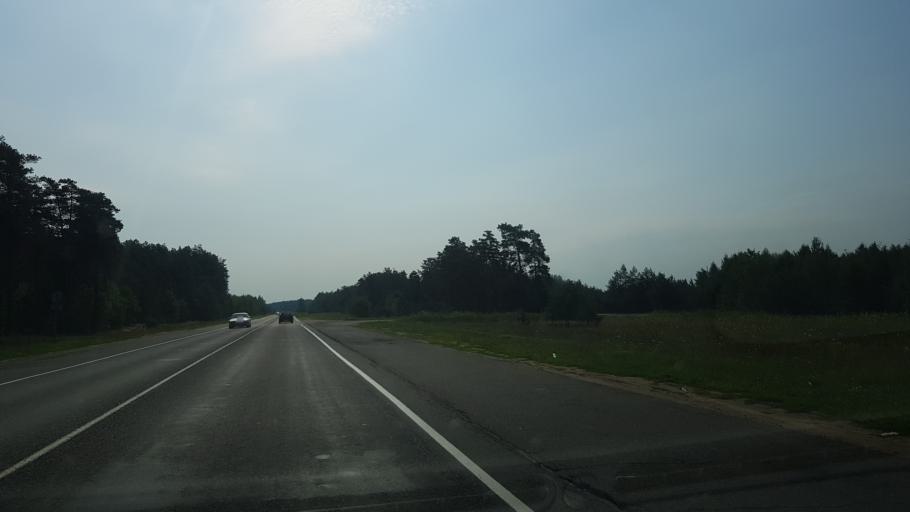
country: BY
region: Mogilev
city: Babruysk
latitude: 53.1655
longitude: 29.2887
